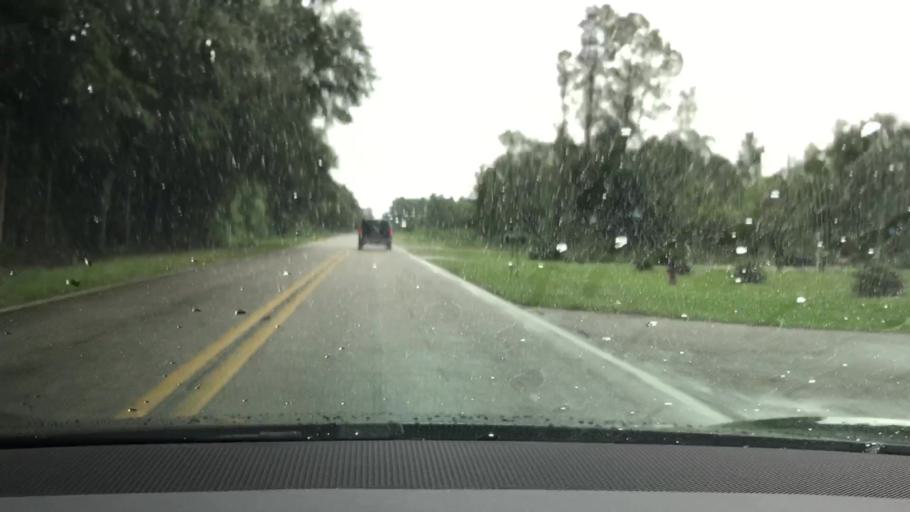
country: US
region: Alabama
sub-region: Geneva County
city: Samson
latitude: 31.1405
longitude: -86.1371
